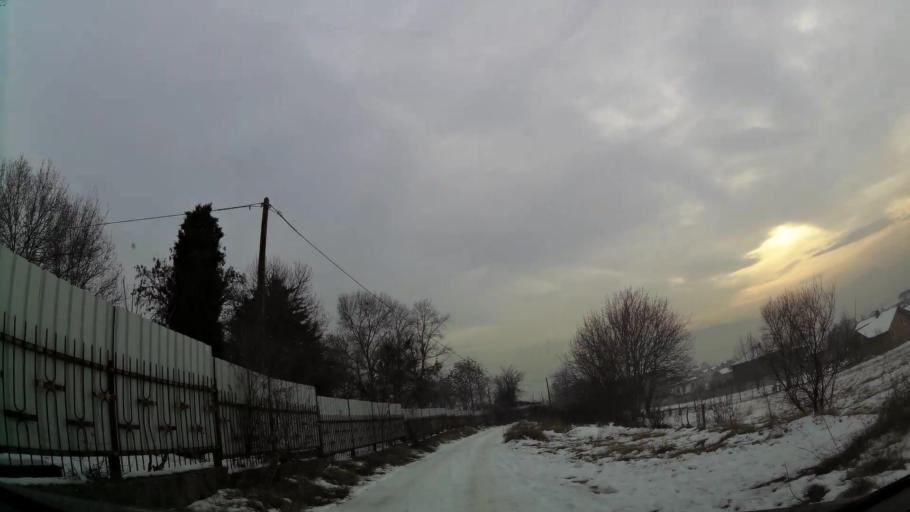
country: MK
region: Suto Orizari
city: Suto Orizare
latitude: 42.0405
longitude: 21.4312
